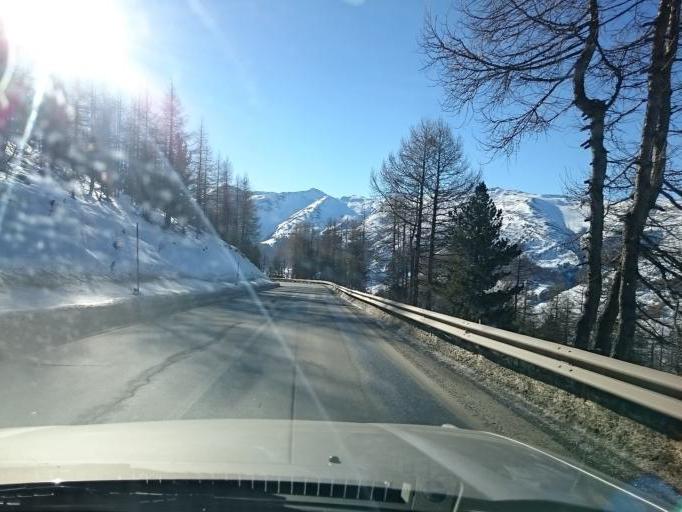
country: IT
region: Lombardy
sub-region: Provincia di Sondrio
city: Livigno
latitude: 46.5370
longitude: 10.1565
